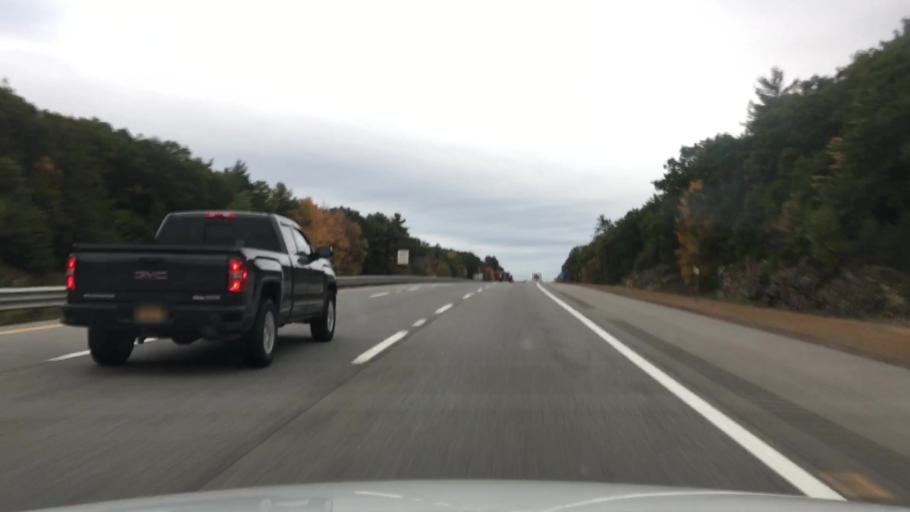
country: US
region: Maine
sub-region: York County
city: Cape Neddick
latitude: 43.1869
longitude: -70.6464
